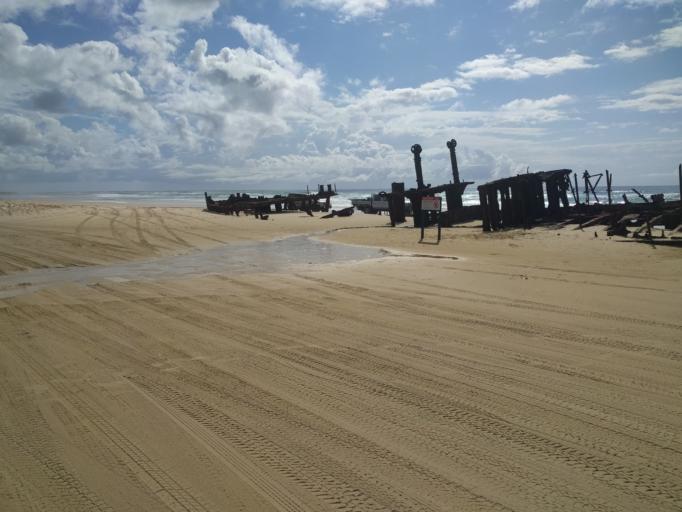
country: AU
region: Queensland
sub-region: Fraser Coast
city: Urangan
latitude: -25.2672
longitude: 153.2382
